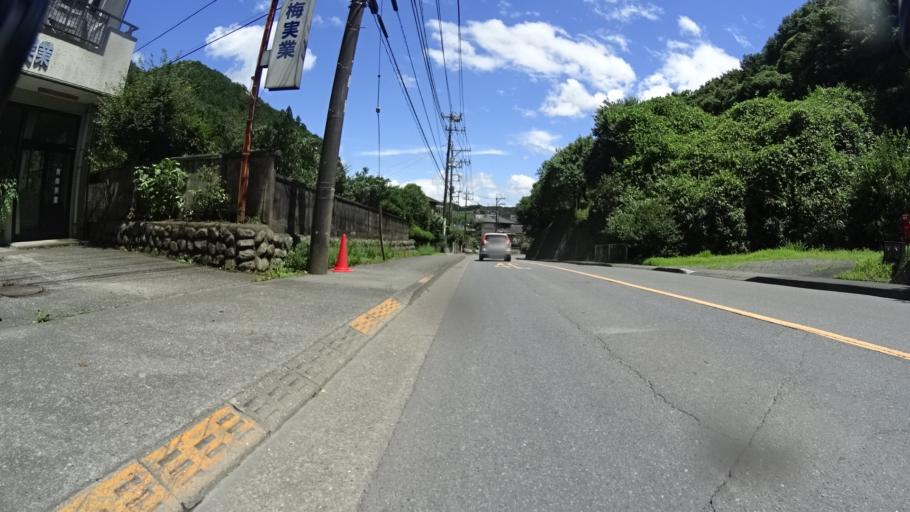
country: JP
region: Tokyo
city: Ome
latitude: 35.8122
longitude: 139.2562
